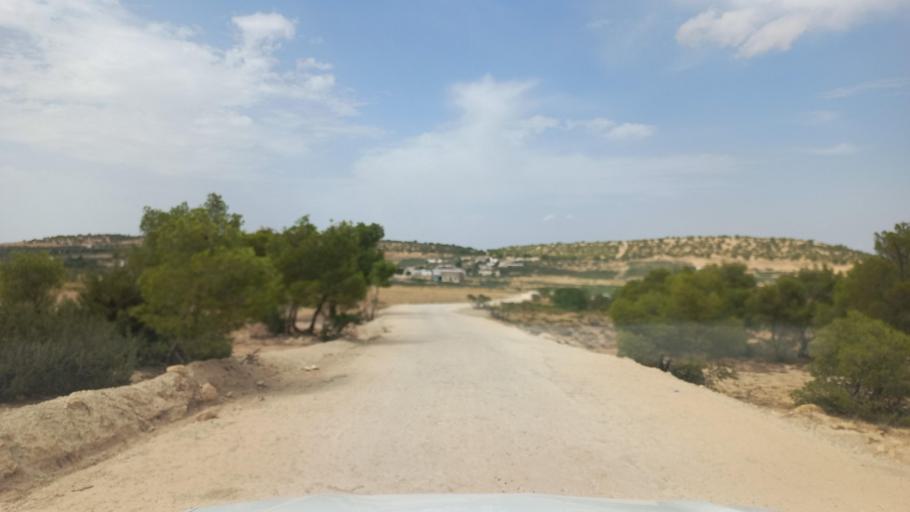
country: TN
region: Al Qasrayn
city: Kasserine
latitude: 35.3855
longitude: 8.8656
